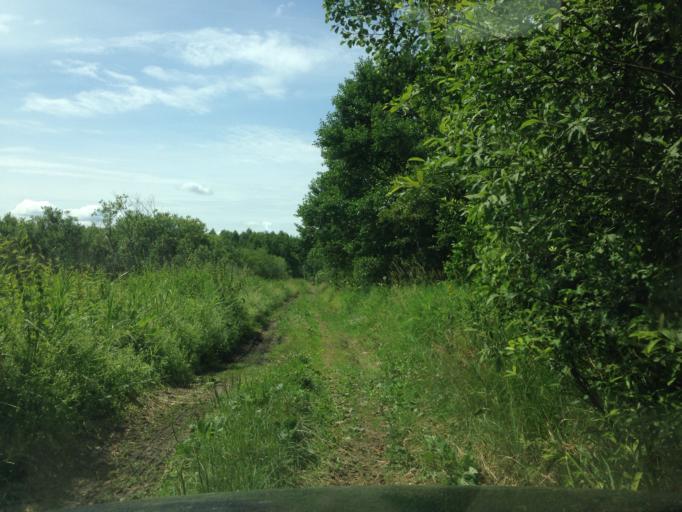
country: PL
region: Kujawsko-Pomorskie
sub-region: Powiat brodnicki
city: Bartniczka
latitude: 53.2704
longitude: 19.5905
